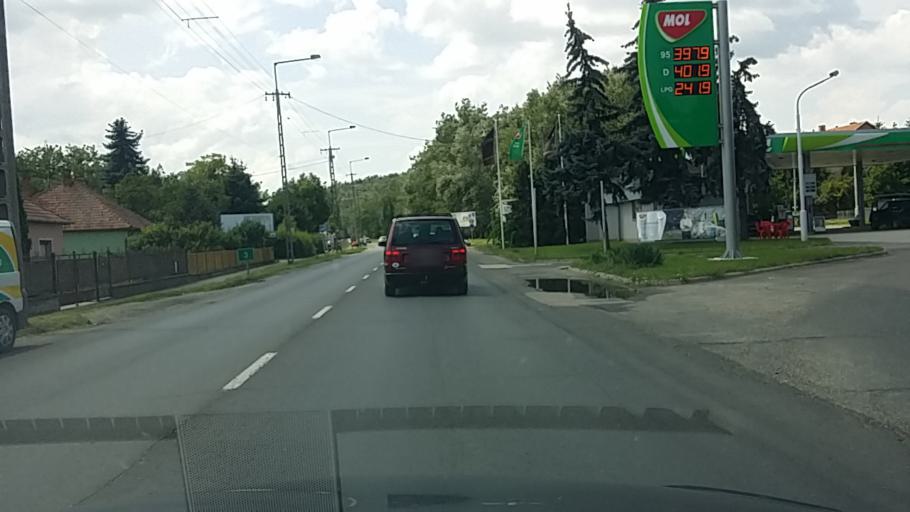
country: HU
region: Bacs-Kiskun
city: Kecskemet
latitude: 46.8906
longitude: 19.6497
